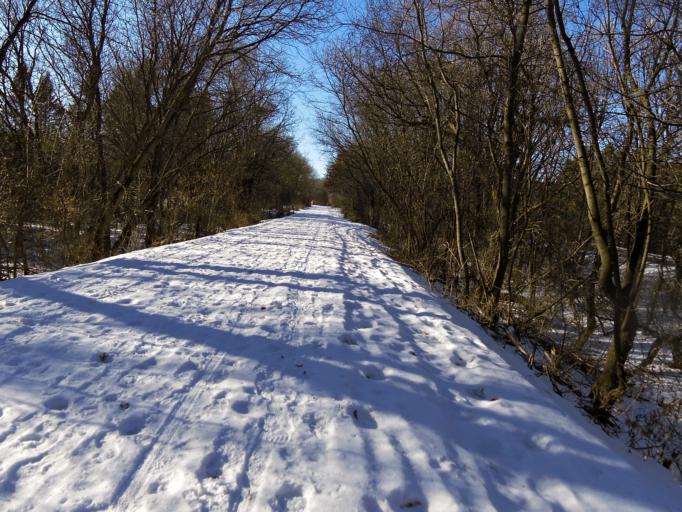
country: US
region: Minnesota
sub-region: Washington County
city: Grant
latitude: 45.0727
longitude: -92.8697
